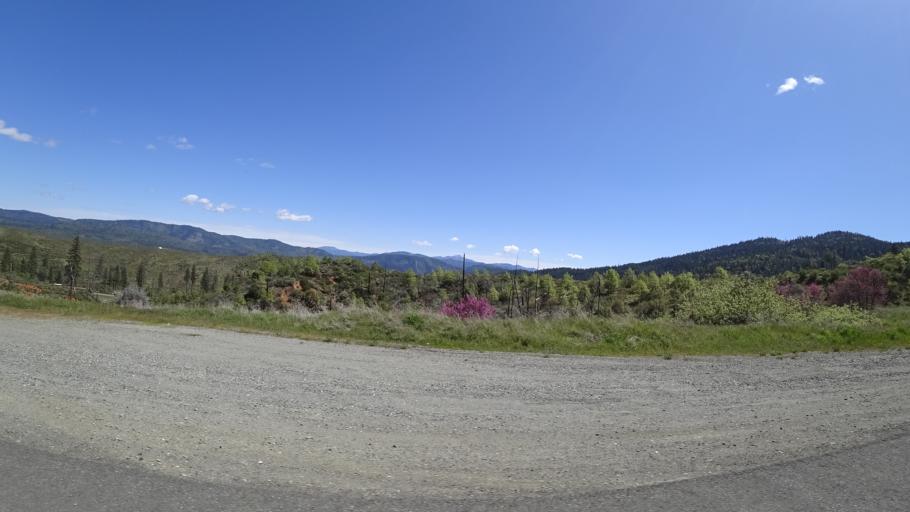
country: US
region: California
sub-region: Trinity County
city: Weaverville
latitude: 40.7448
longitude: -122.9755
